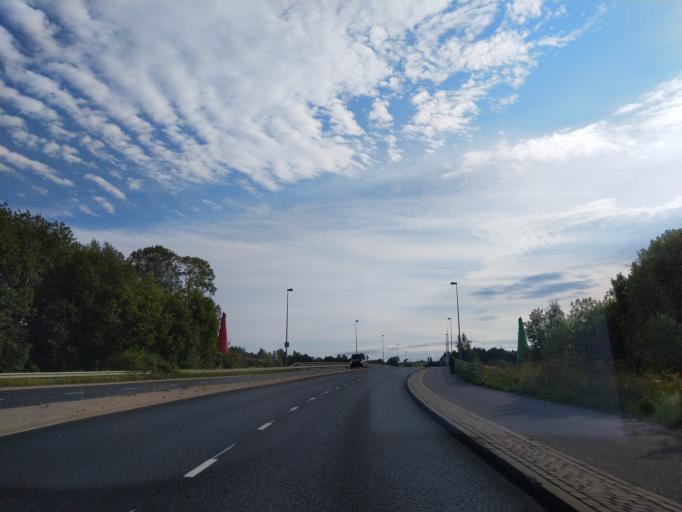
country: FI
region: Varsinais-Suomi
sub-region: Turku
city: Turku
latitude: 60.4241
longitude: 22.2389
